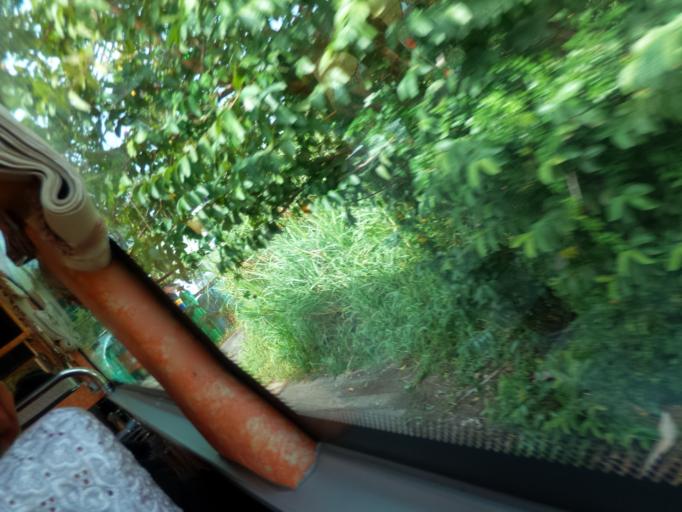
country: TW
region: Taiwan
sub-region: Hsinchu
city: Hsinchu
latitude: 24.7621
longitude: 120.9841
